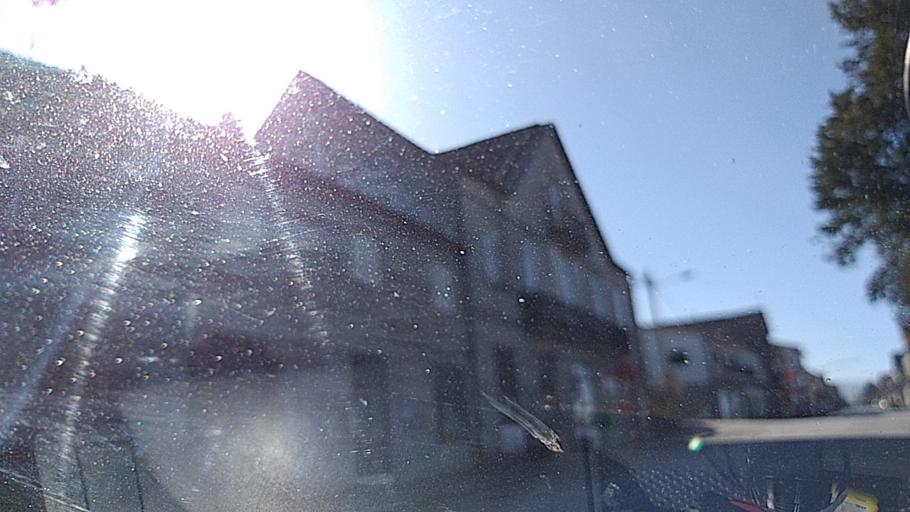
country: PT
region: Guarda
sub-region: Celorico da Beira
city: Celorico da Beira
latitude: 40.6668
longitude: -7.3811
